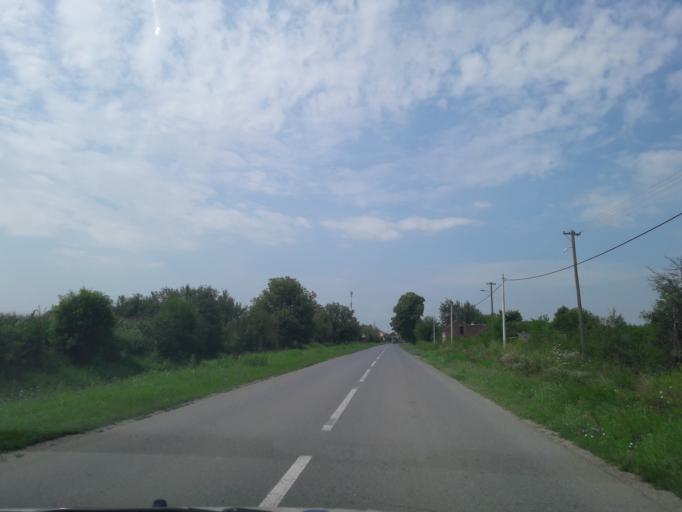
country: HR
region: Osjecko-Baranjska
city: Gorjani
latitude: 45.4912
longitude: 18.4039
